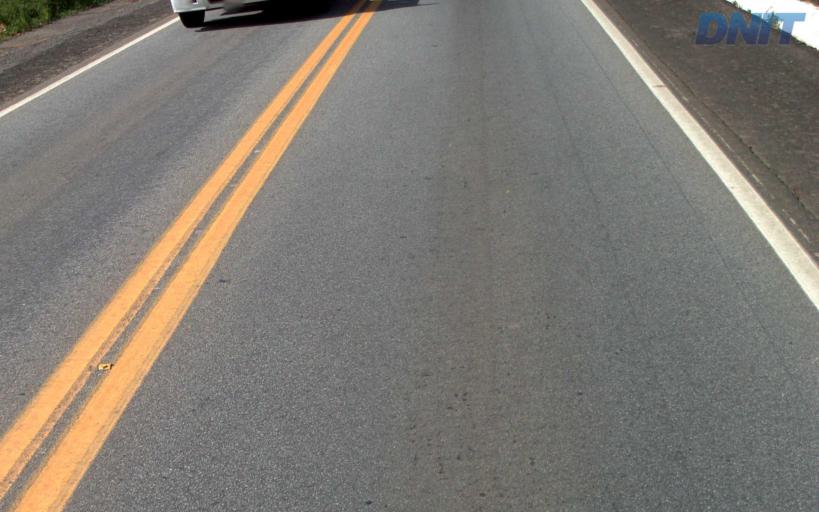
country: BR
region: Minas Gerais
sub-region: Ipaba
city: Ipaba
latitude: -19.4067
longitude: -42.4861
